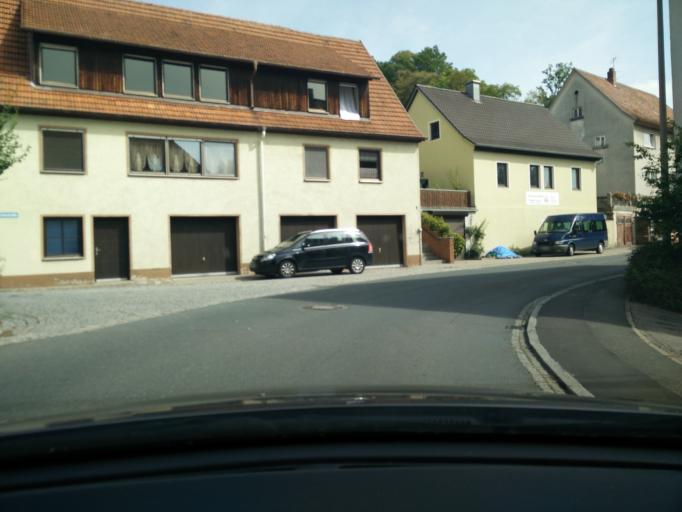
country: DE
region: Bavaria
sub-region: Regierungsbezirk Mittelfranken
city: Wilhelmsdorf
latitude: 49.5635
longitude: 10.7399
